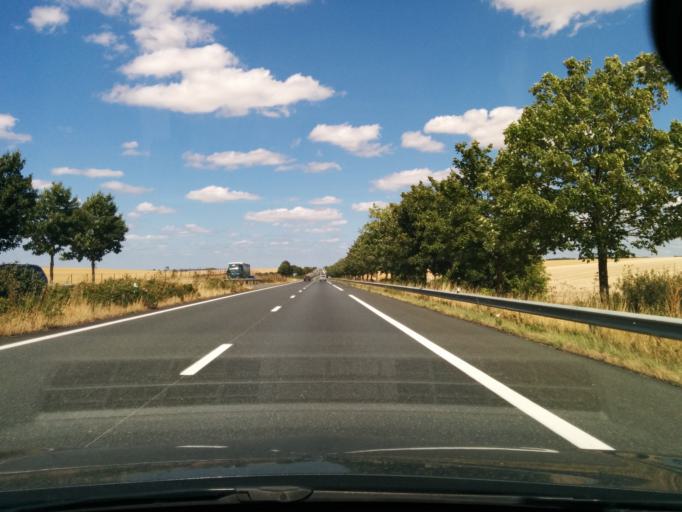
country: FR
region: Centre
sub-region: Departement de l'Indre
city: Vatan
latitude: 47.0062
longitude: 1.7798
